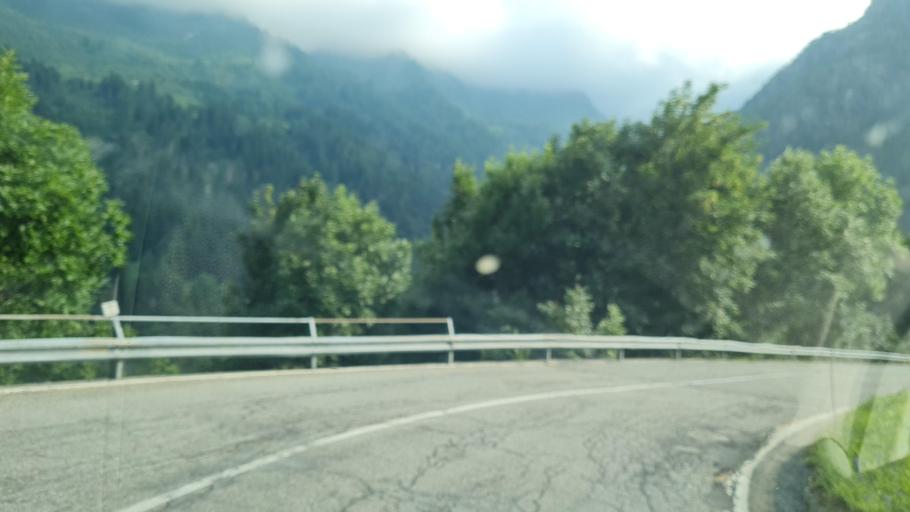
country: IT
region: Aosta Valley
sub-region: Valle d'Aosta
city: Champorcher
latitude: 45.6217
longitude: 7.6421
